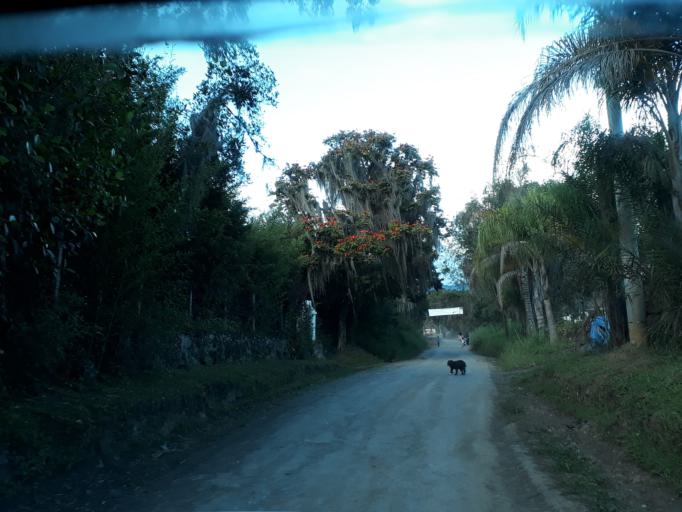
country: CO
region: Cundinamarca
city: Pacho
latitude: 5.1505
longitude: -74.1559
